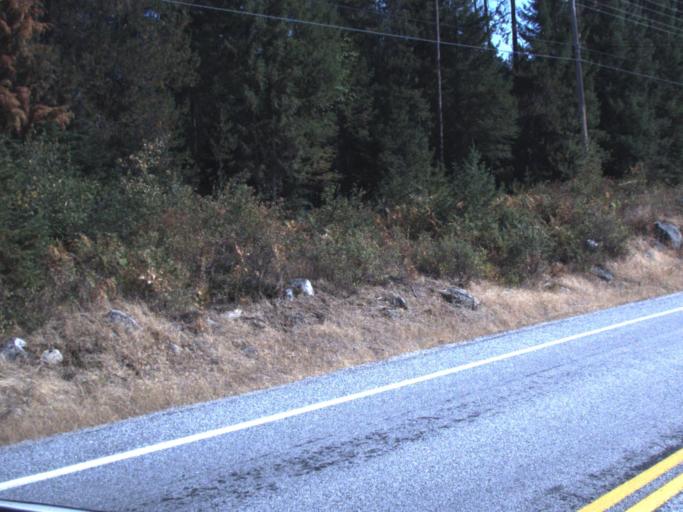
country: US
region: Washington
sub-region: Pend Oreille County
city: Newport
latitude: 48.1670
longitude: -117.3003
